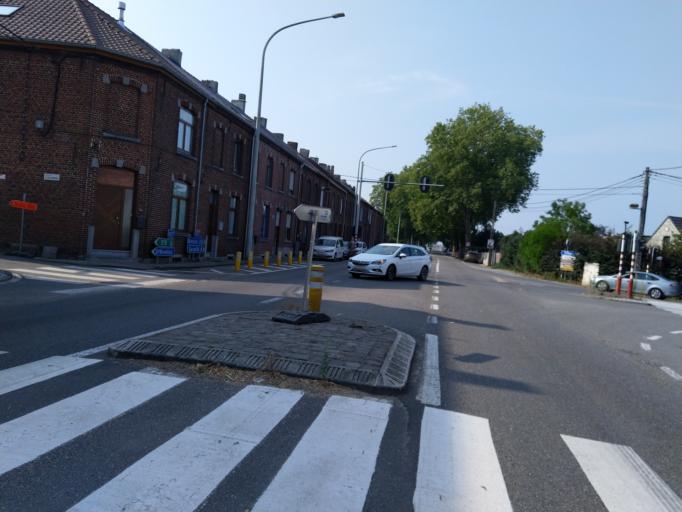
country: BE
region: Wallonia
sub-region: Province du Hainaut
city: Seneffe
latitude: 50.5615
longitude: 4.2787
